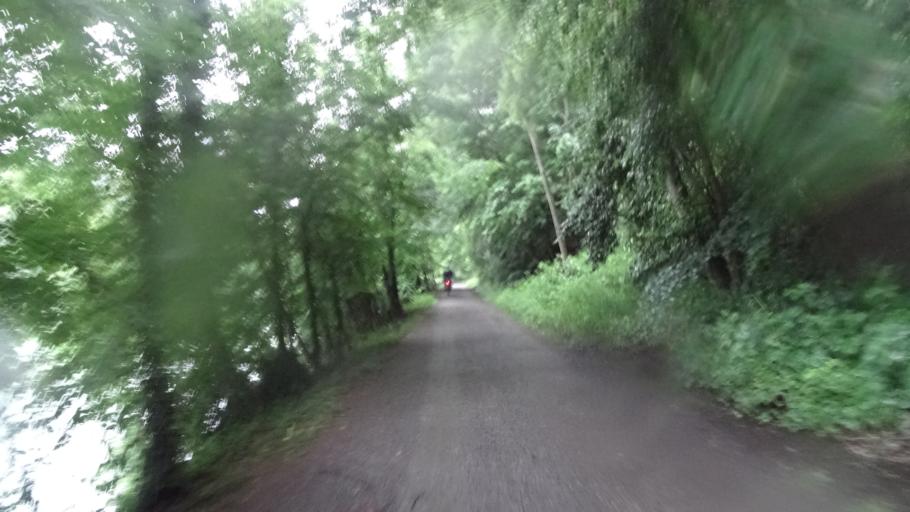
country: AT
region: Upper Austria
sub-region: Politischer Bezirk Scharding
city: Scharding
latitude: 48.5023
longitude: 13.4507
